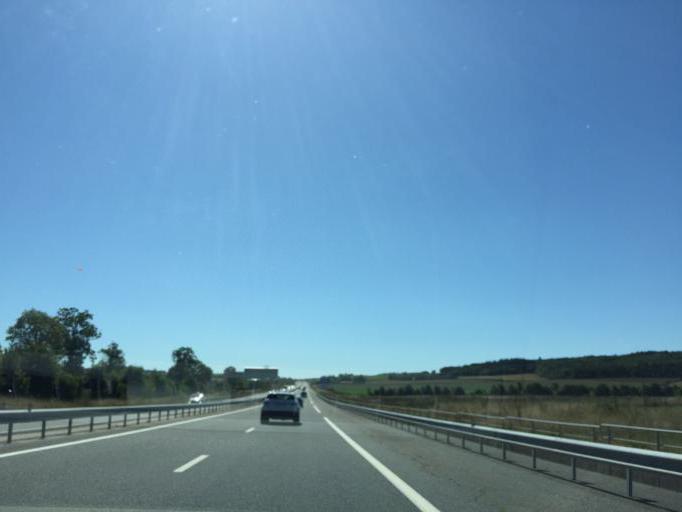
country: FR
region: Midi-Pyrenees
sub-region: Departement de l'Aveyron
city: La Cavalerie
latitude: 43.9928
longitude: 3.1742
